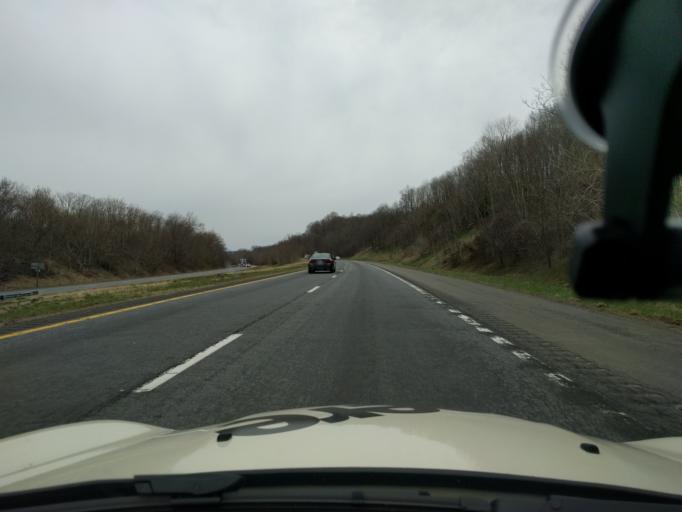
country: US
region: Virginia
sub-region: Warren County
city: Shenandoah Farms
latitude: 38.9097
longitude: -77.9755
